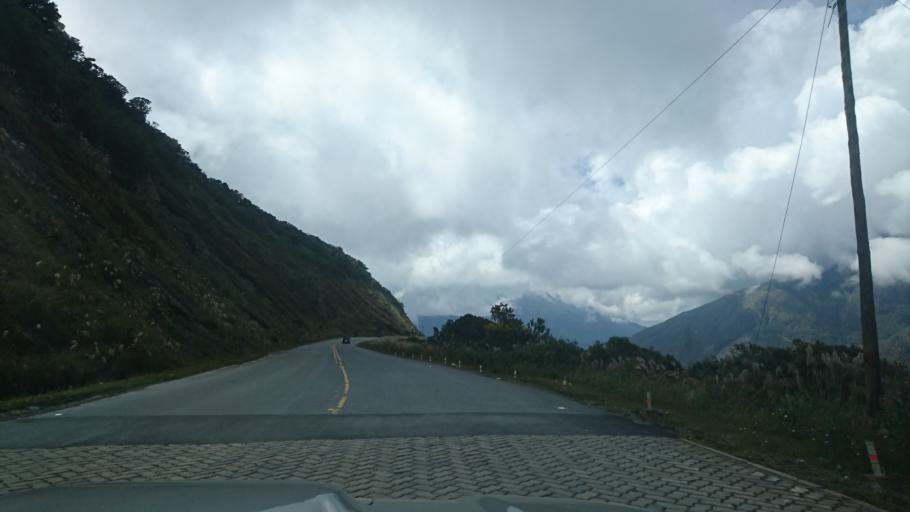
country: BO
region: La Paz
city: Coroico
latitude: -16.2905
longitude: -67.8710
